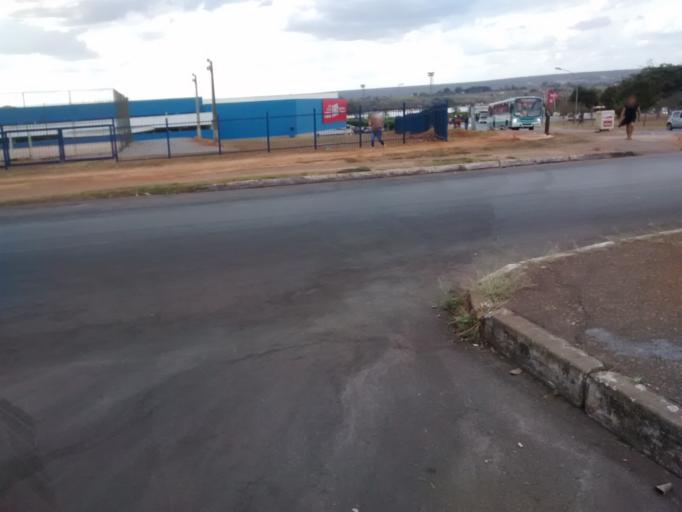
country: BR
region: Federal District
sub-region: Brasilia
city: Brasilia
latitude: -15.7382
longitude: -47.8995
